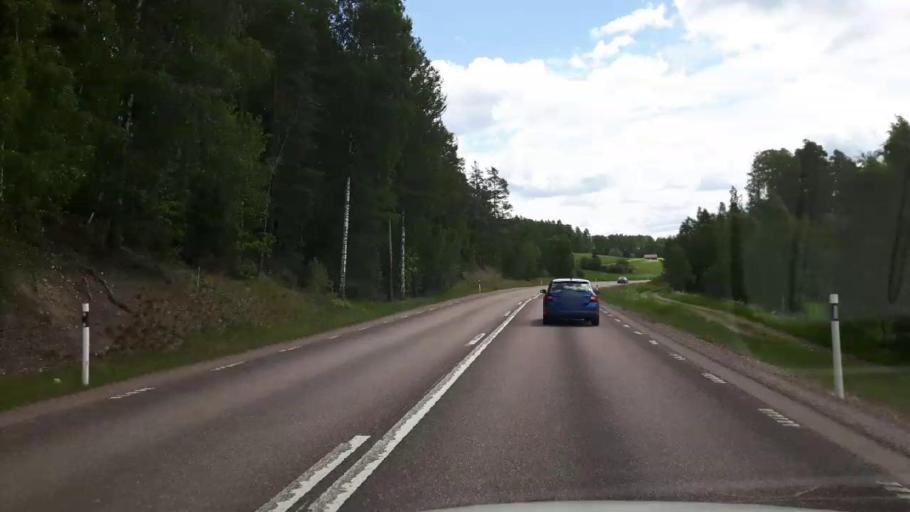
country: SE
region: Dalarna
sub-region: Saters Kommun
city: Saeter
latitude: 60.4344
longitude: 15.8271
